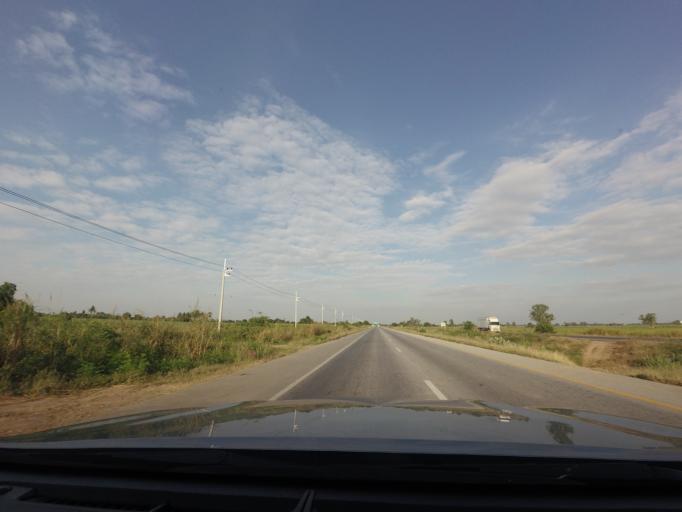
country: TH
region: Nakhon Sawan
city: Nakhon Sawan
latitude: 15.7608
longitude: 100.0964
